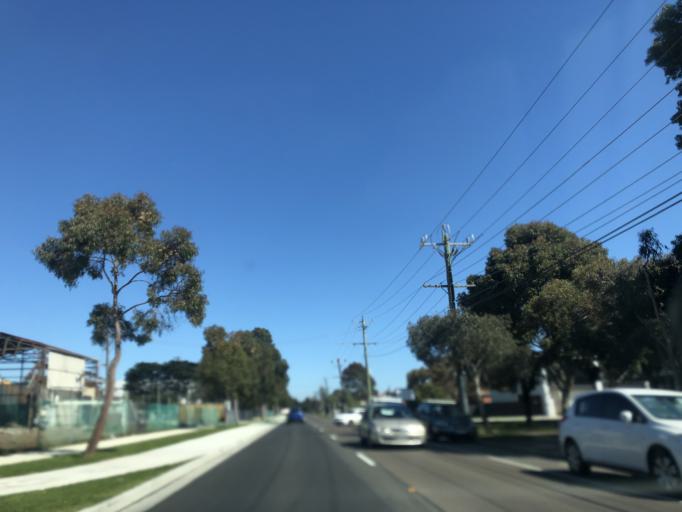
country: AU
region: Victoria
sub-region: Monash
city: Clayton
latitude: -37.9037
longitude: 145.1285
